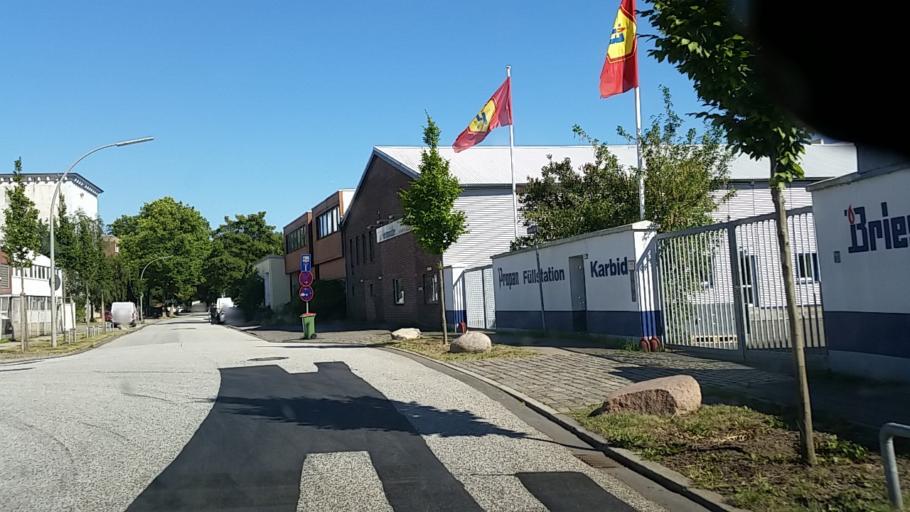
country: DE
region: Hamburg
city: Rothenburgsort
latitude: 53.5455
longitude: 10.0485
